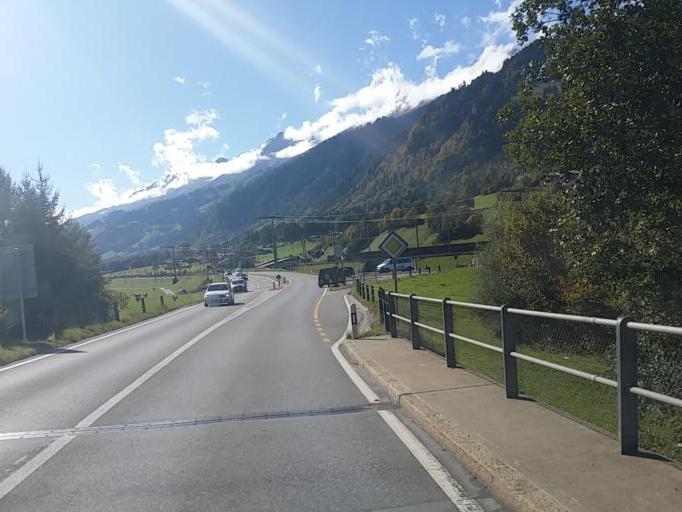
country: CH
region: Bern
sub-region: Frutigen-Niedersimmental District
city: Aeschi
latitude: 46.6189
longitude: 7.6837
